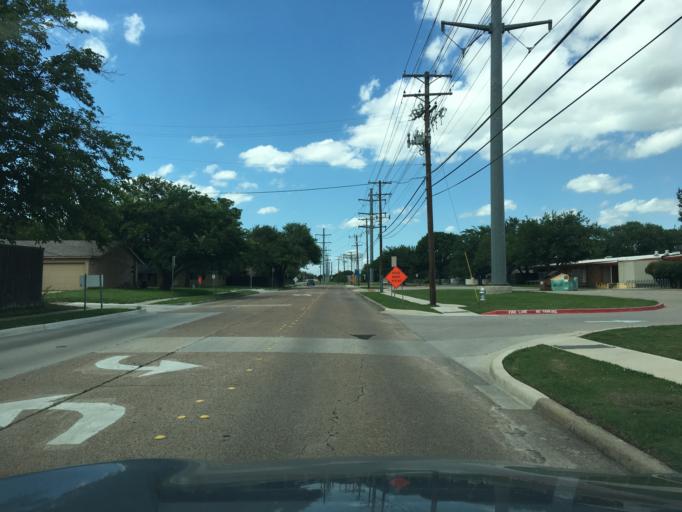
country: US
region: Texas
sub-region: Dallas County
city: Richardson
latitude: 32.9477
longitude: -96.7050
